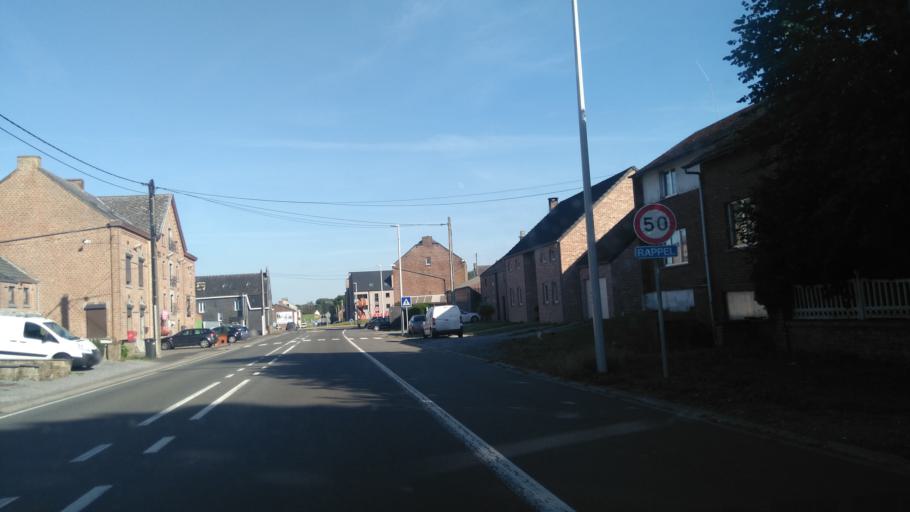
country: BE
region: Wallonia
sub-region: Province de Namur
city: Forville
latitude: 50.5567
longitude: 5.0345
